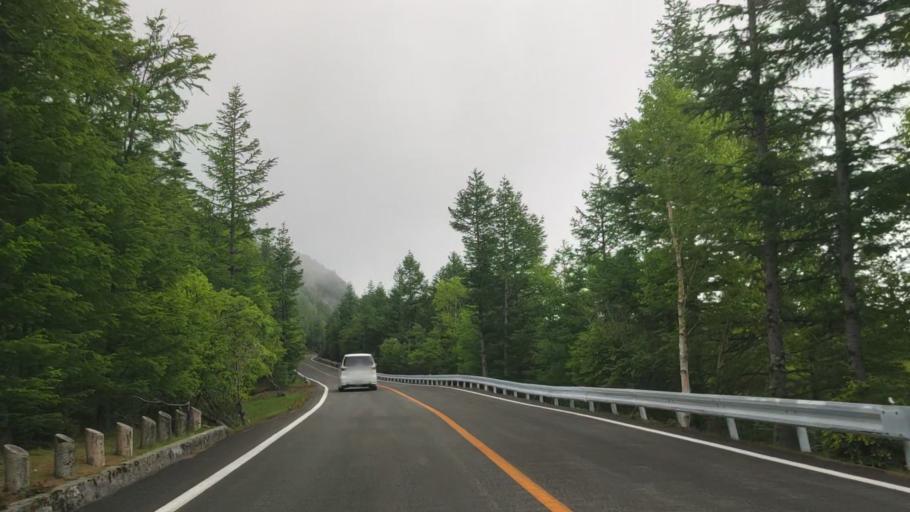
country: JP
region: Yamanashi
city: Fujikawaguchiko
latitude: 35.3873
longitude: 138.6984
